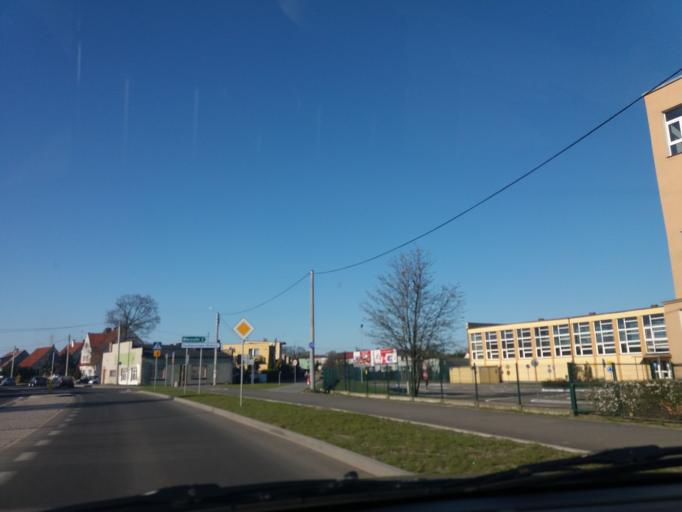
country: PL
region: Warmian-Masurian Voivodeship
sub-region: Powiat nidzicki
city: Nidzica
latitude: 53.3671
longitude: 20.4295
